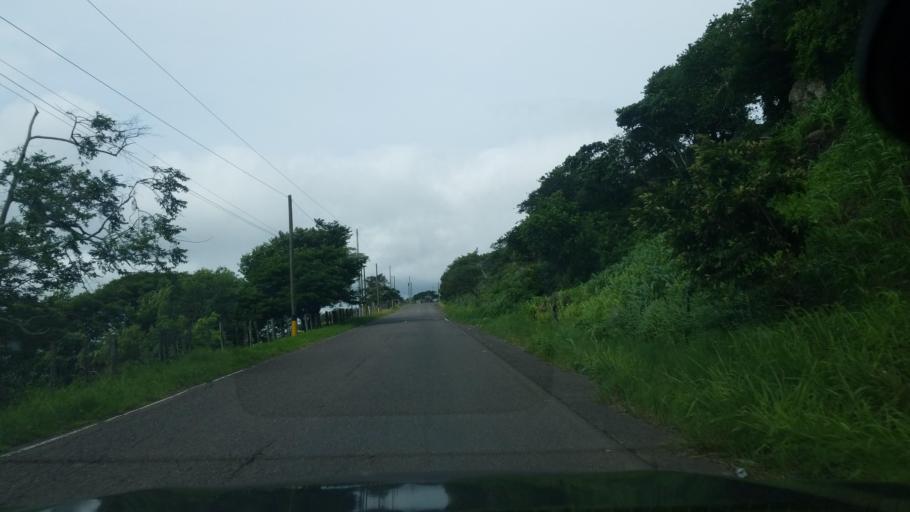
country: HN
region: Choluteca
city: San Marcos de Colon
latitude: 13.3712
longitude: -86.9198
